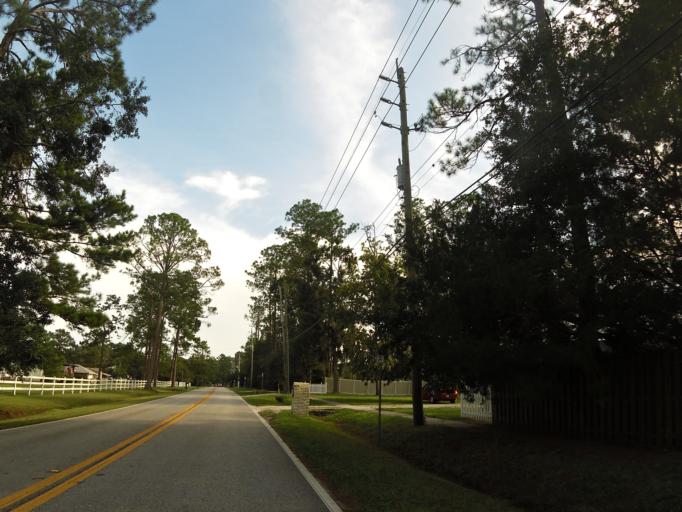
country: US
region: Florida
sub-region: Saint Johns County
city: Fruit Cove
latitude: 30.1429
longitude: -81.5957
